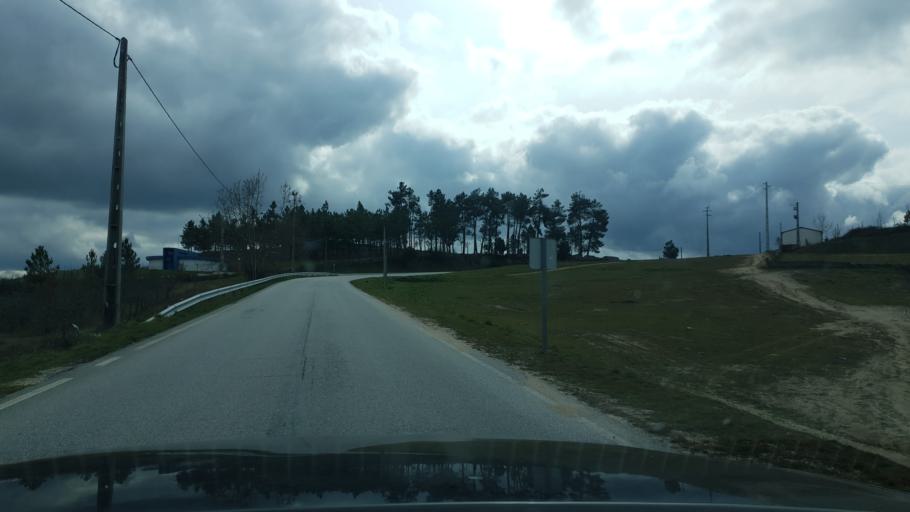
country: PT
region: Viseu
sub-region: Moimenta da Beira
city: Moimenta da Beira
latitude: 40.9563
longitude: -7.5829
